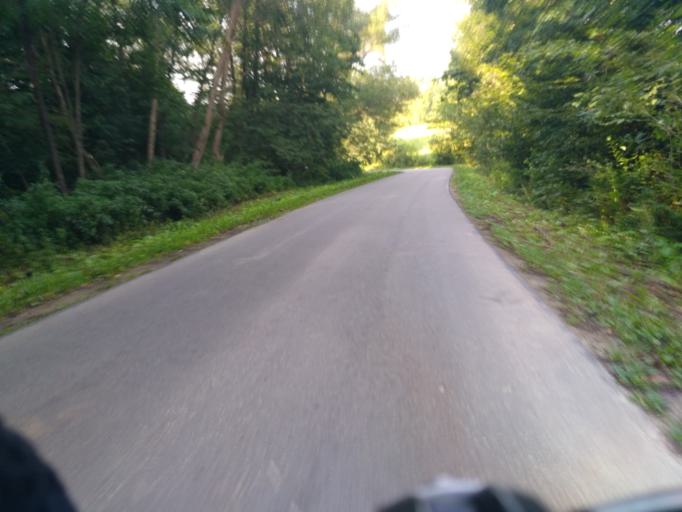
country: PL
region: Subcarpathian Voivodeship
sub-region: Powiat brzozowski
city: Golcowa
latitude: 49.7861
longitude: 22.0165
